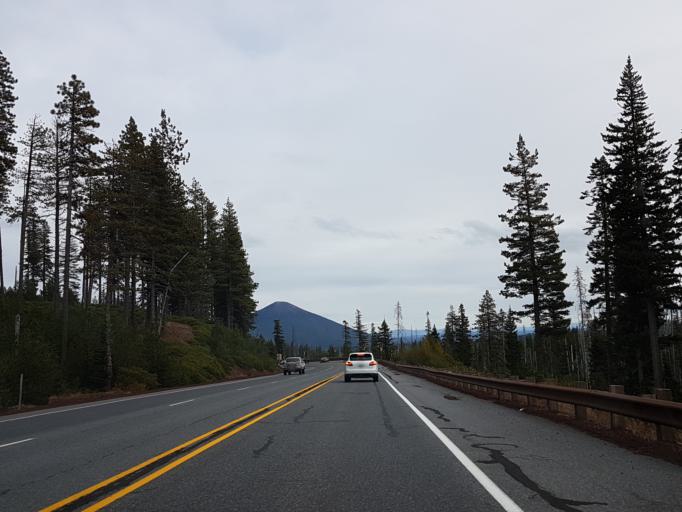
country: US
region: Oregon
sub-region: Deschutes County
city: Sisters
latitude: 44.4235
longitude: -121.8070
